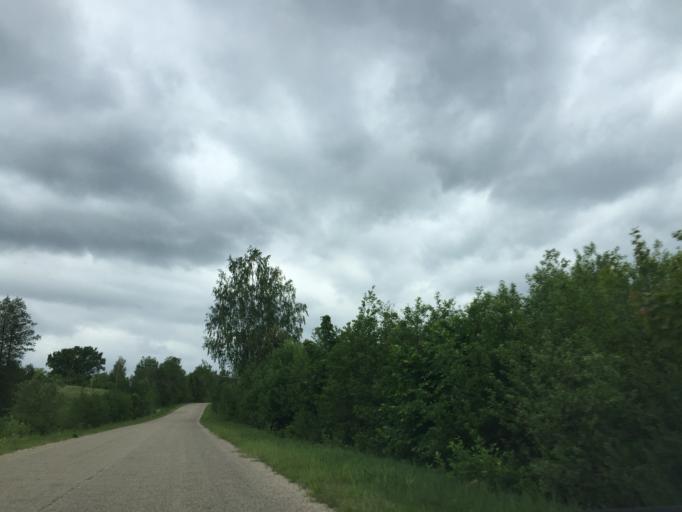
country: LV
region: Aglona
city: Aglona
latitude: 56.0905
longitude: 26.9432
